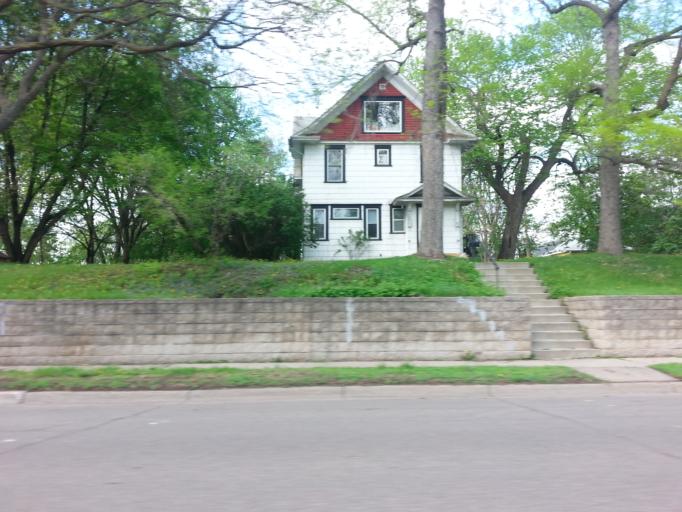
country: US
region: Minnesota
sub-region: Ramsey County
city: Saint Paul
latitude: 44.9487
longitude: -93.0487
